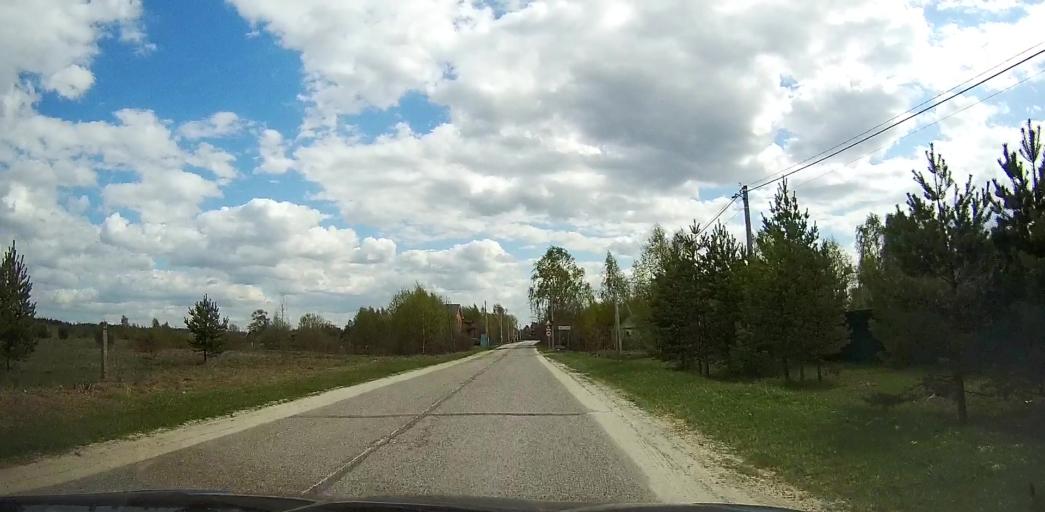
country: RU
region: Moskovskaya
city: Davydovo
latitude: 55.6408
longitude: 38.7761
